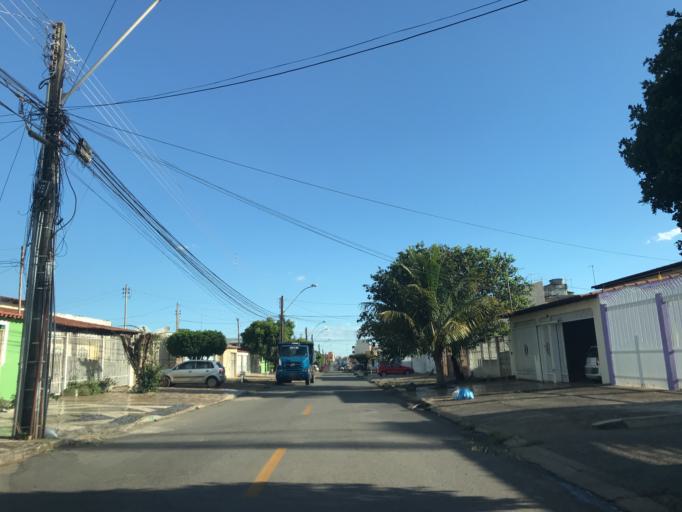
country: BR
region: Federal District
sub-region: Brasilia
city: Brasilia
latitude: -15.8143
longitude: -48.0628
